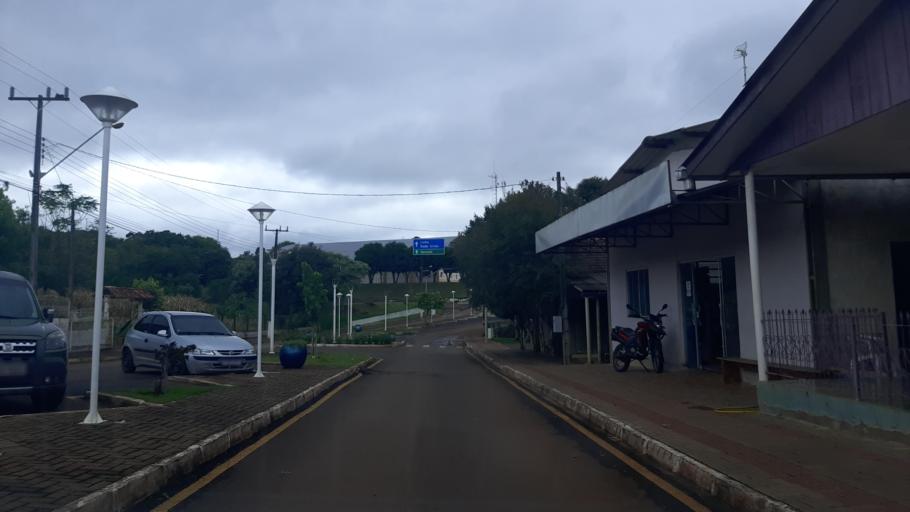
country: BR
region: Parana
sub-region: Ampere
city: Ampere
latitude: -26.0344
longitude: -53.4856
